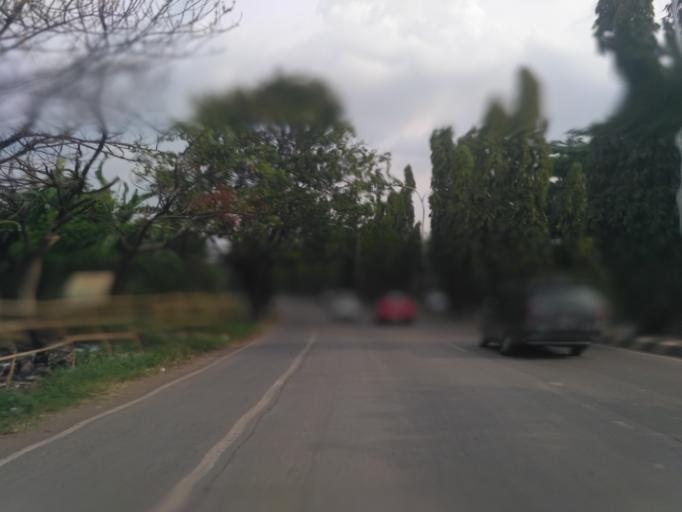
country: ID
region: Central Java
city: Semarang
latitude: -6.9731
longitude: 110.3882
